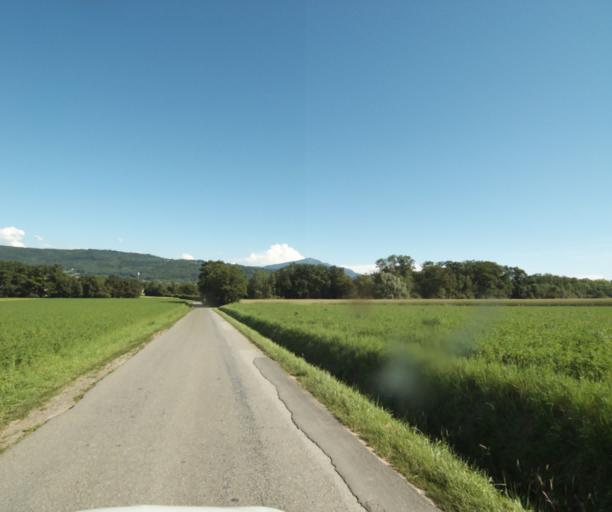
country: FR
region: Rhone-Alpes
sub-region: Departement de la Haute-Savoie
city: Douvaine
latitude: 46.3285
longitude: 6.3120
